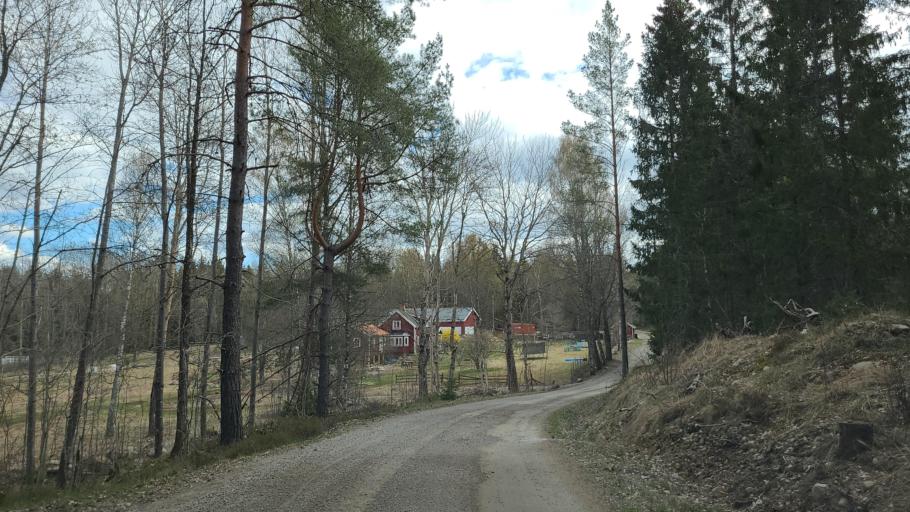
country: SE
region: OEstergoetland
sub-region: Norrkopings Kommun
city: Krokek
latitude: 58.6851
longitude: 16.4206
